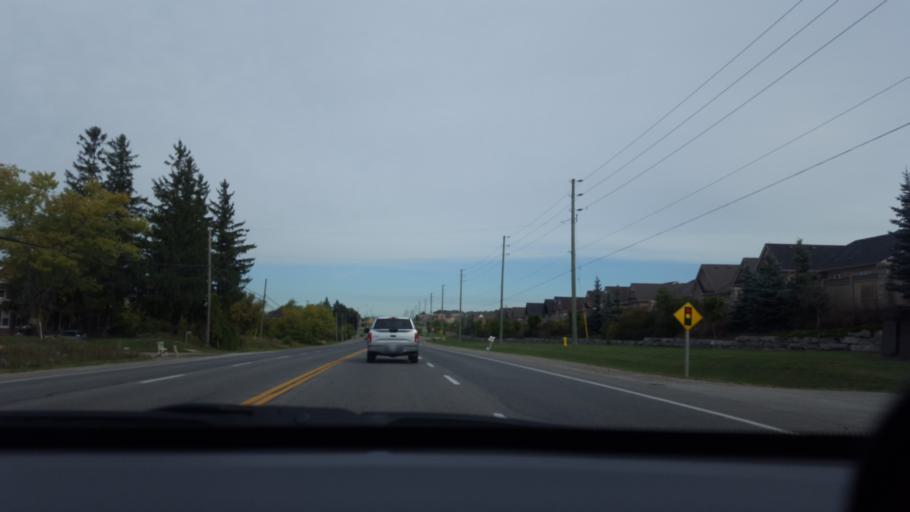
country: CA
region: Ontario
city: Vaughan
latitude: 43.8846
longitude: -79.5193
